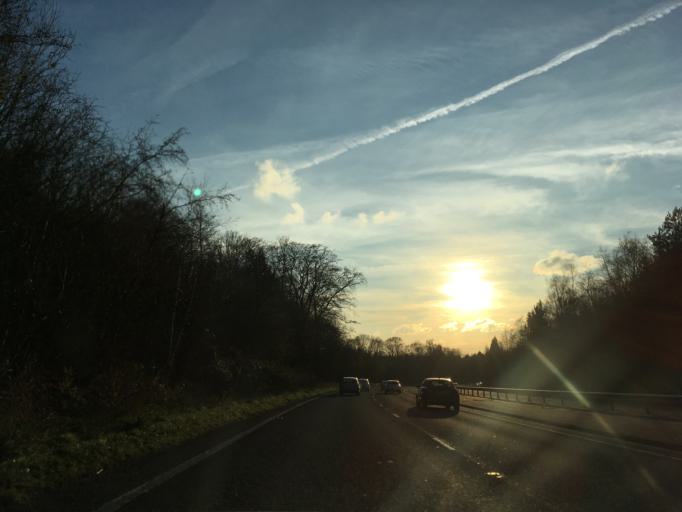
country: GB
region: England
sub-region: Cheshire East
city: Wilmslow
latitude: 53.3422
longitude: -2.2002
